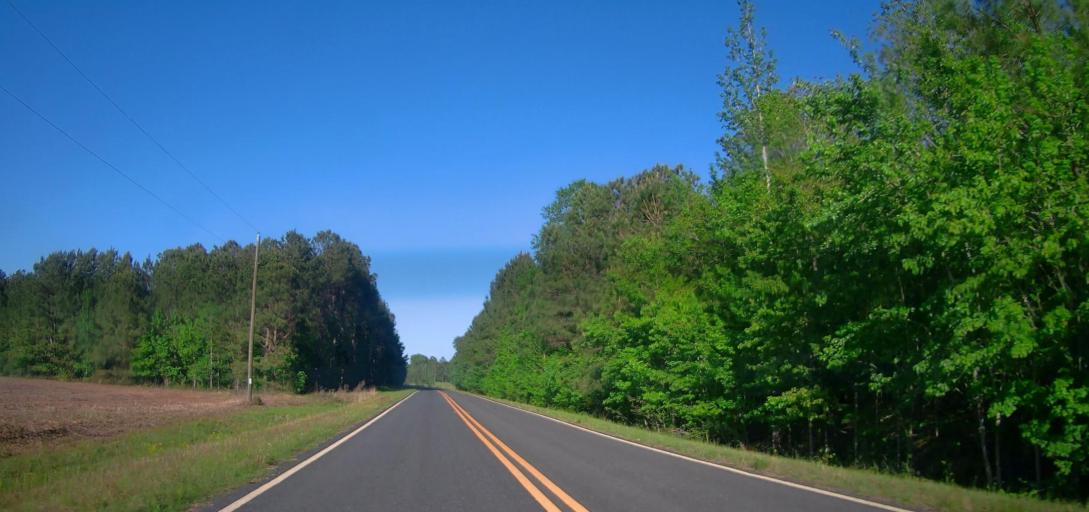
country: US
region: Georgia
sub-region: Macon County
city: Marshallville
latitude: 32.3849
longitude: -83.8590
